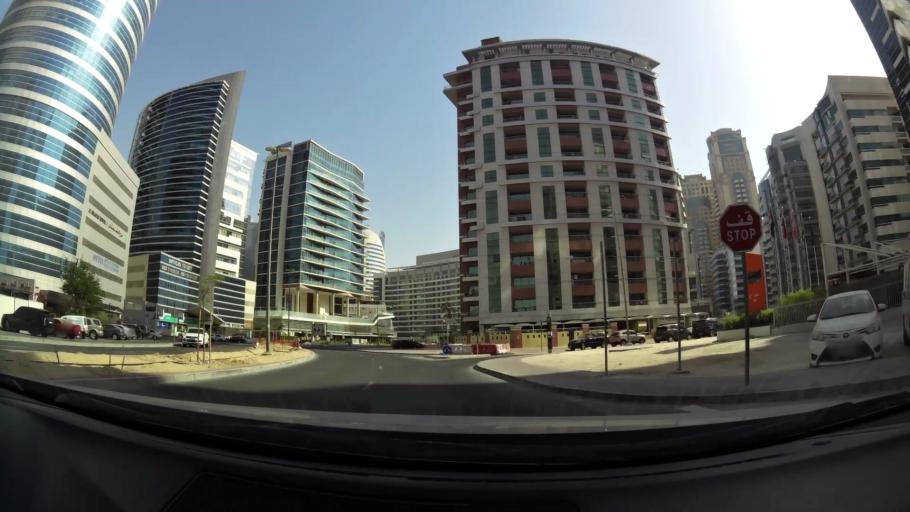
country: AE
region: Dubai
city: Dubai
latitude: 25.0990
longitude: 55.1737
